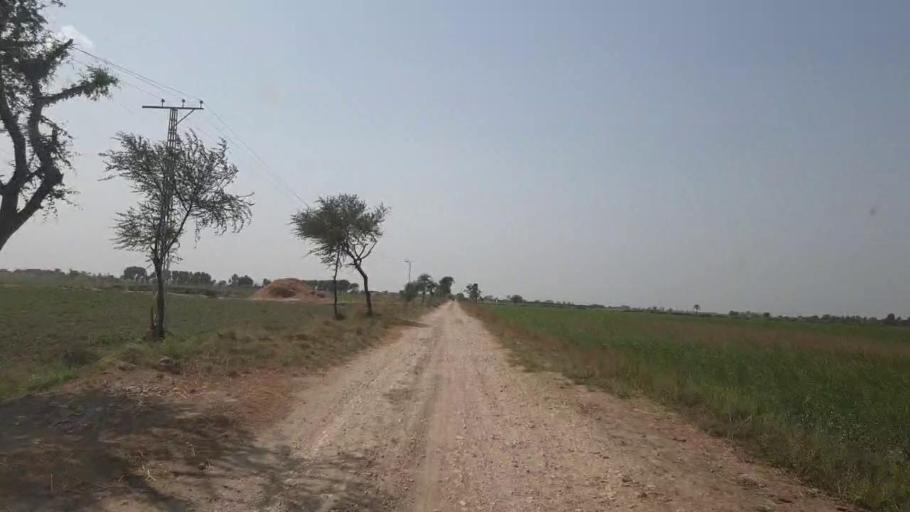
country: PK
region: Sindh
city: Jati
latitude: 24.4920
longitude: 68.5380
